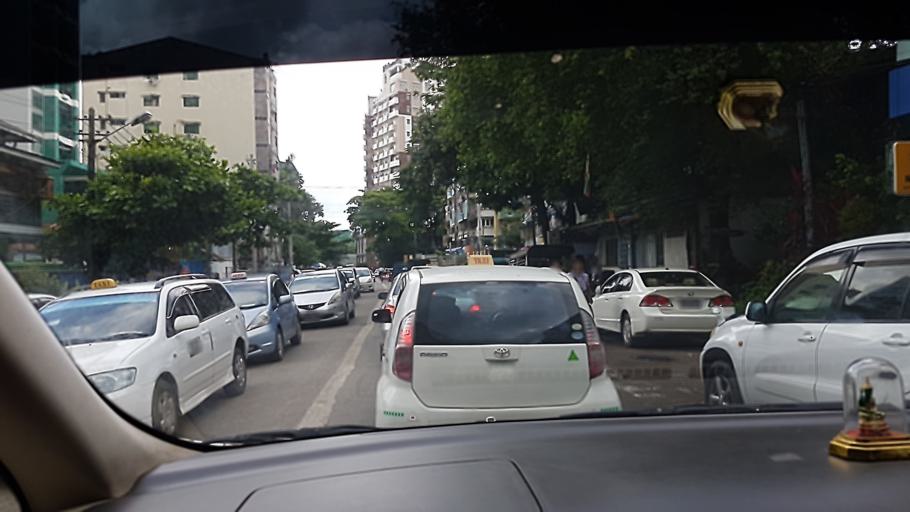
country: MM
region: Yangon
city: Yangon
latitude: 16.8018
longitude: 96.1300
